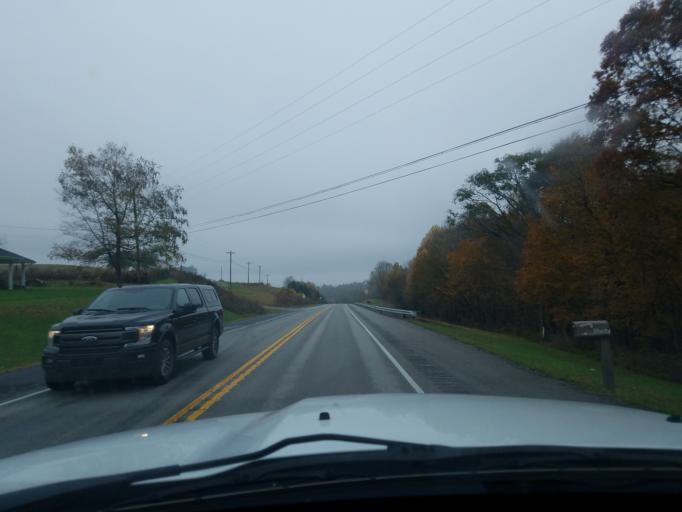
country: US
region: Kentucky
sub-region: Taylor County
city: Campbellsville
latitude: 37.3870
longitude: -85.4210
